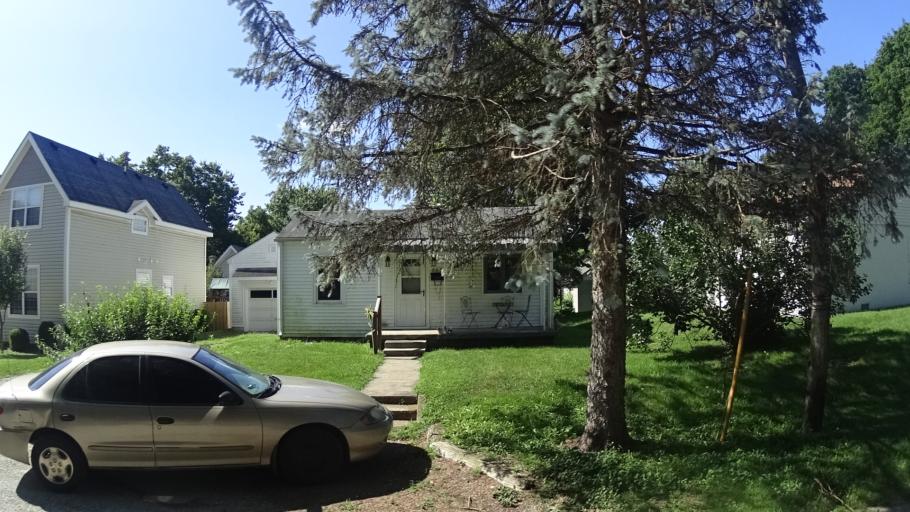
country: US
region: Indiana
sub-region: Madison County
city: Pendleton
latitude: 39.9986
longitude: -85.7499
